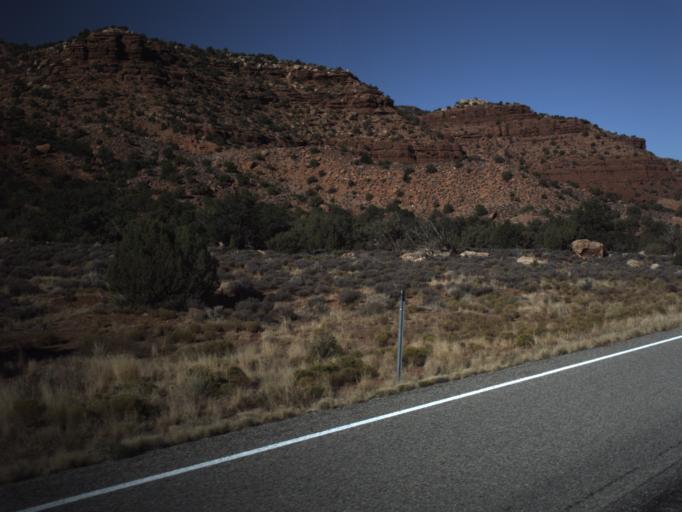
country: US
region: Utah
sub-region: San Juan County
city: Blanding
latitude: 37.6666
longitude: -110.1955
